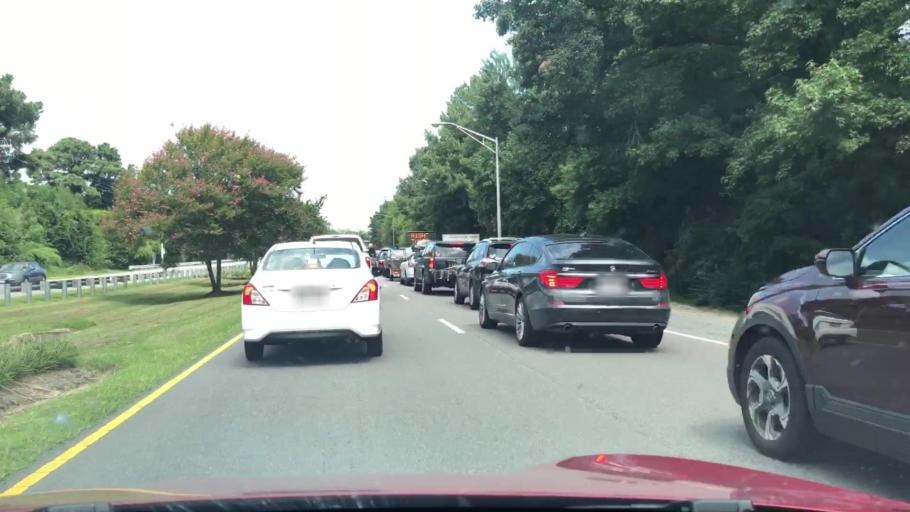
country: US
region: Virginia
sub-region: City of Virginia Beach
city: Virginia Beach
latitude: 36.9072
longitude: -76.1296
